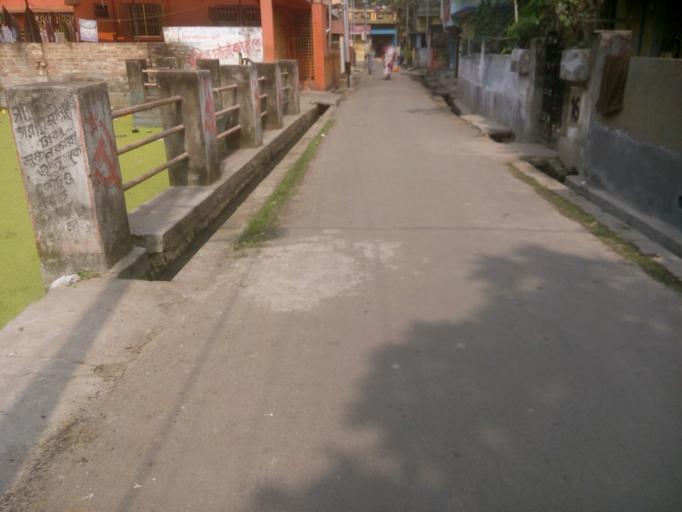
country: IN
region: West Bengal
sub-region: South 24 Paraganas
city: Santoshpur
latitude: 22.4620
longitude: 88.3076
